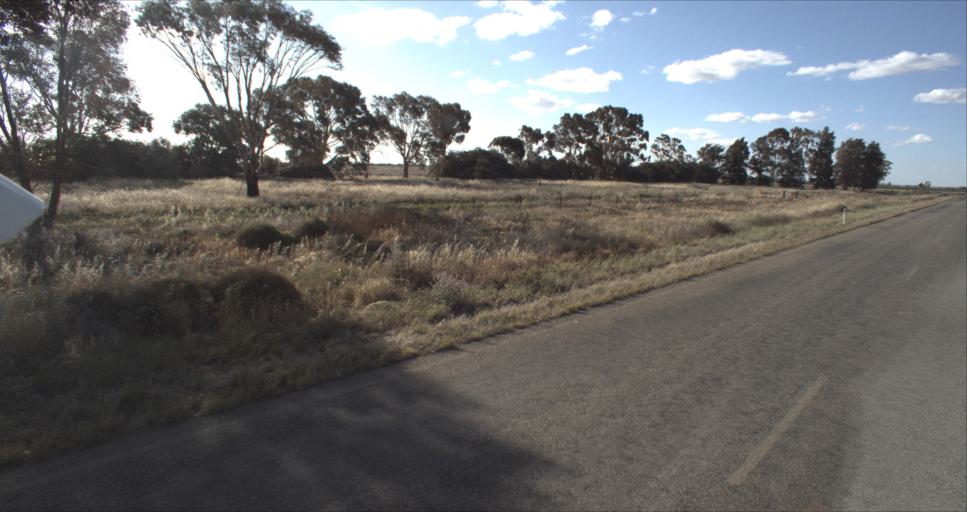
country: AU
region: New South Wales
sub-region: Leeton
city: Leeton
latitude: -34.5397
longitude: 146.2800
